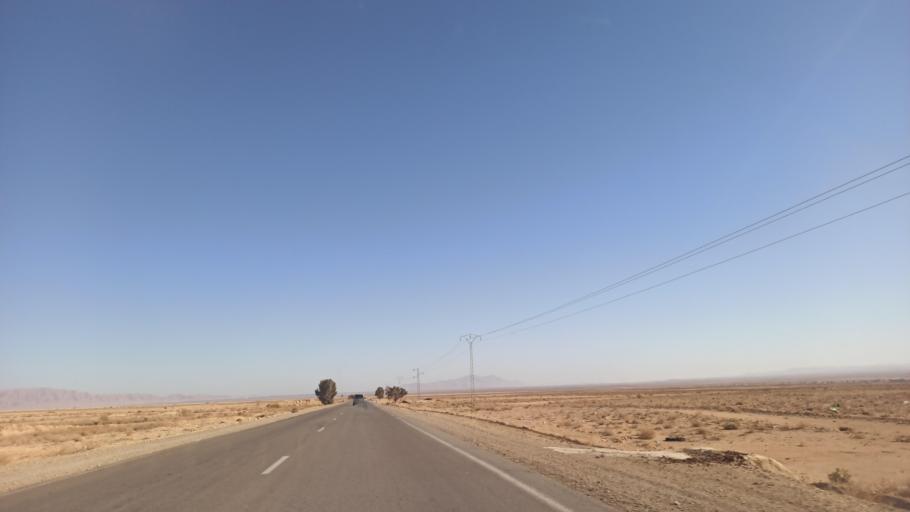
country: TN
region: Gafsa
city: Al Metlaoui
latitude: 34.3182
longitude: 8.5107
